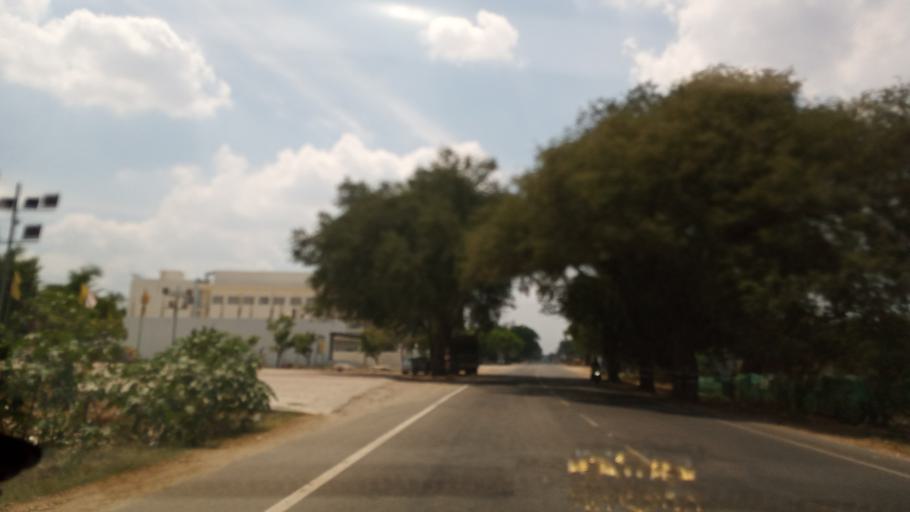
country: IN
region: Tamil Nadu
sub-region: Vellore
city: Walajapet
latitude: 12.9201
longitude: 79.3806
